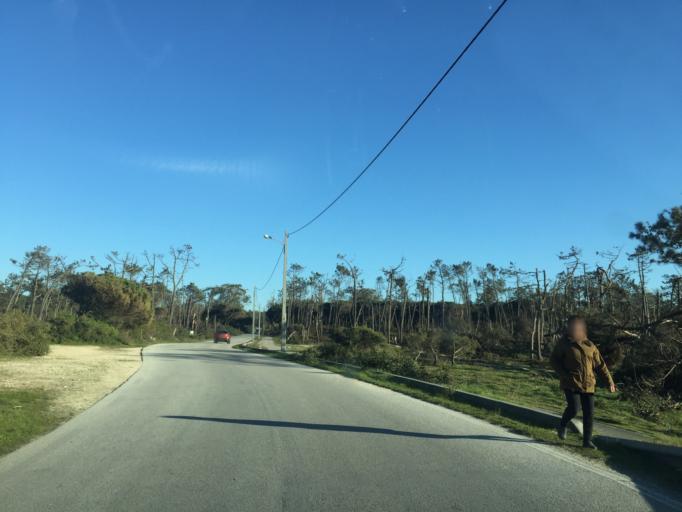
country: PT
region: Coimbra
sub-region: Figueira da Foz
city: Lavos
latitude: 40.0875
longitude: -8.8728
